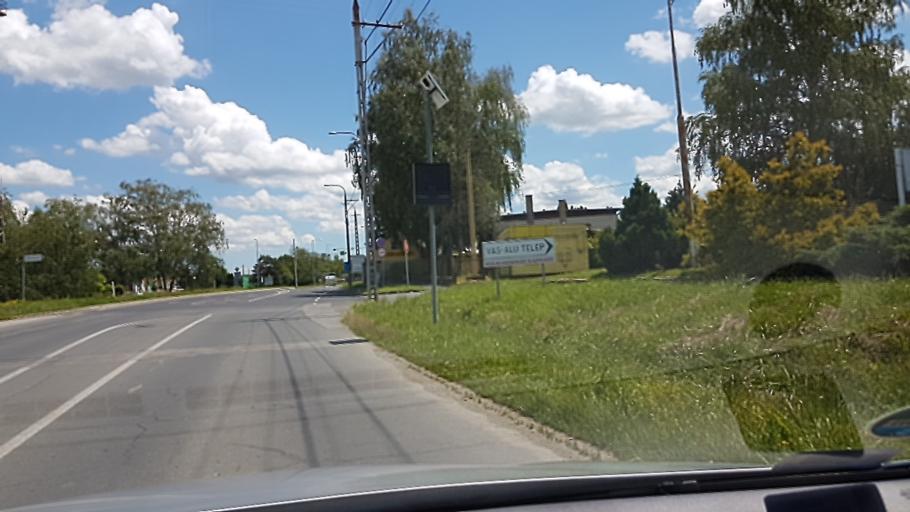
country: HU
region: Zala
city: Zalaegerszeg
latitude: 46.8535
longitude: 16.8105
